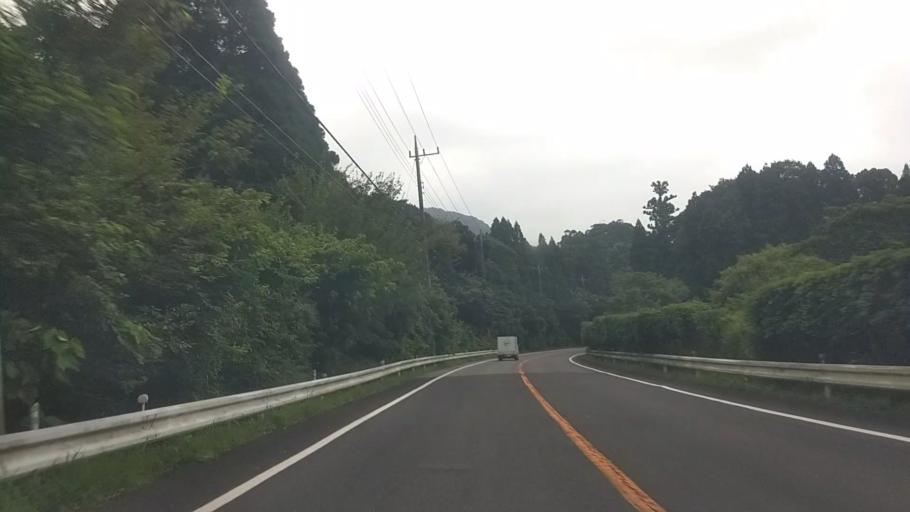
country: JP
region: Chiba
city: Kawaguchi
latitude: 35.1494
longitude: 140.0680
